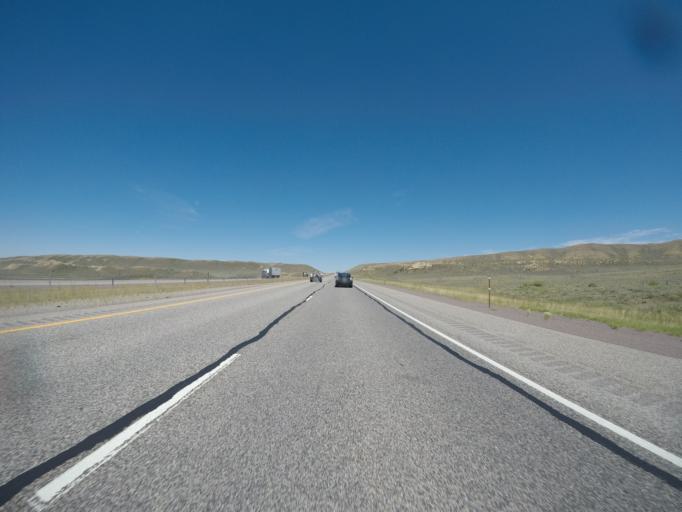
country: US
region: Wyoming
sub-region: Carbon County
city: Saratoga
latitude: 41.7484
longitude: -106.5018
